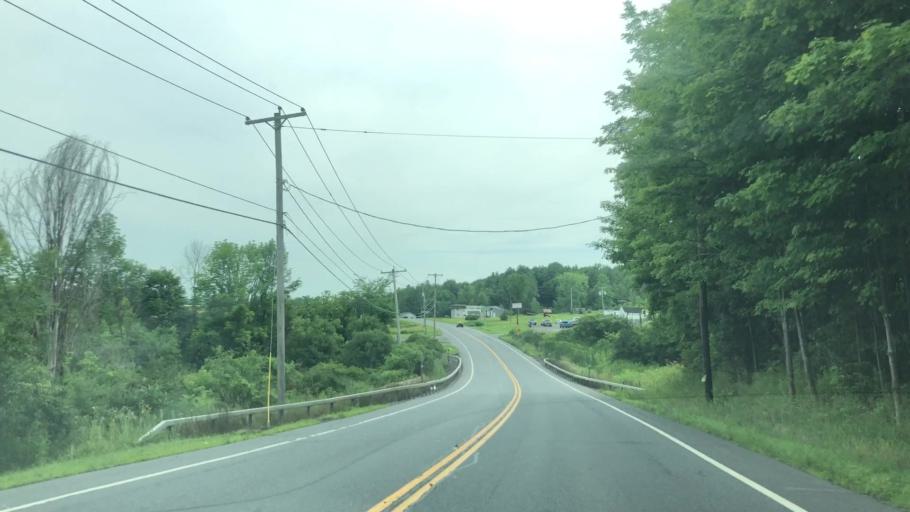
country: US
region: New York
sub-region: Washington County
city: Whitehall
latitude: 43.5289
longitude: -73.4131
